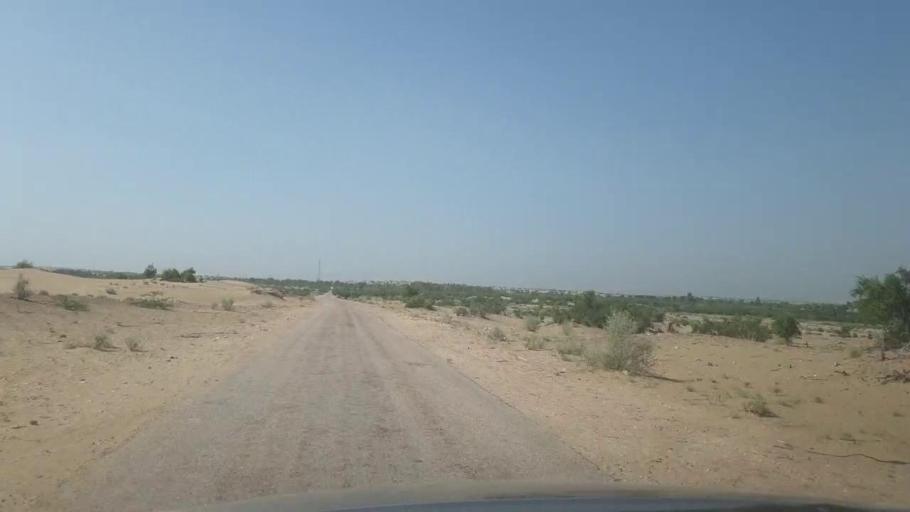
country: PK
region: Sindh
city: Rohri
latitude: 27.4221
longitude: 69.0797
